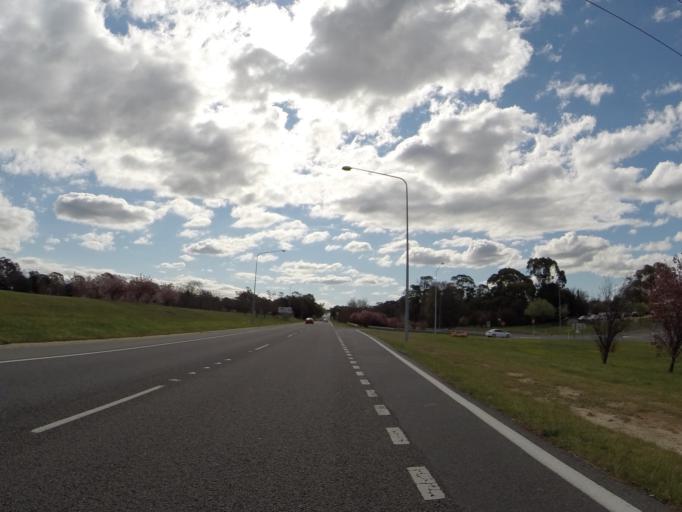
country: AU
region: Australian Capital Territory
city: Belconnen
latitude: -35.1950
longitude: 149.0866
